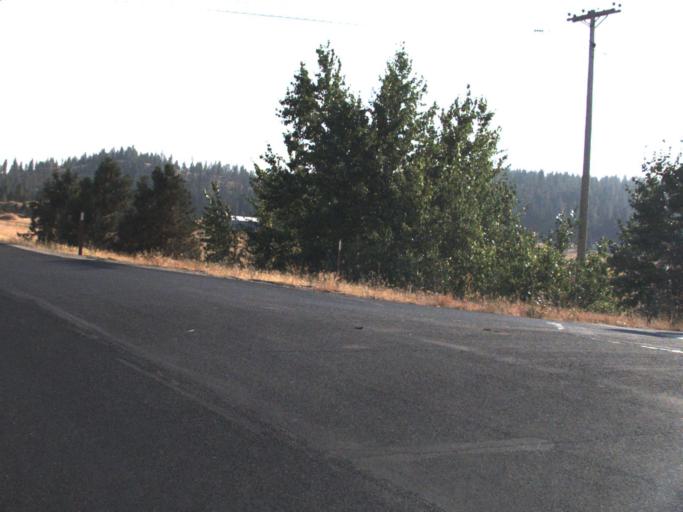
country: US
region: Washington
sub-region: Spokane County
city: Deer Park
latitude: 48.0605
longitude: -117.3449
